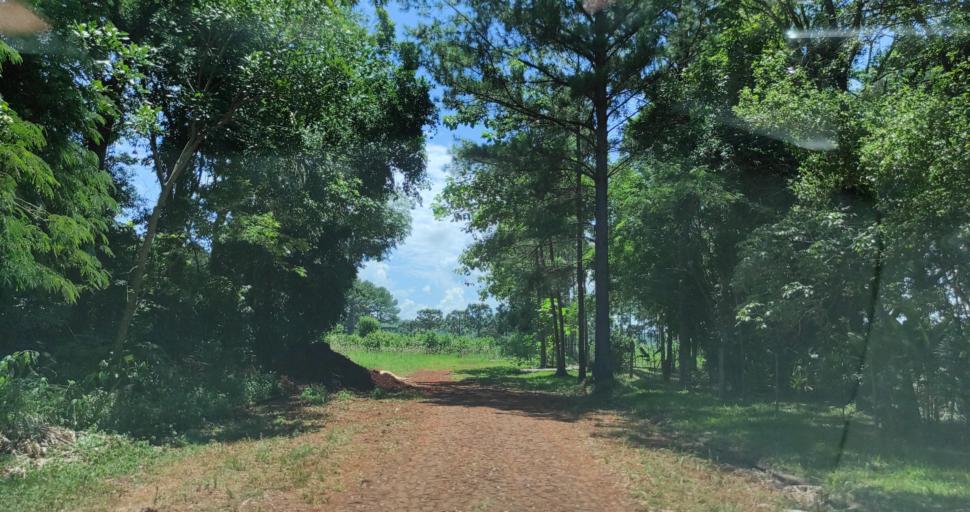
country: AR
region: Misiones
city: Ruiz de Montoya
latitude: -26.9854
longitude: -55.0472
